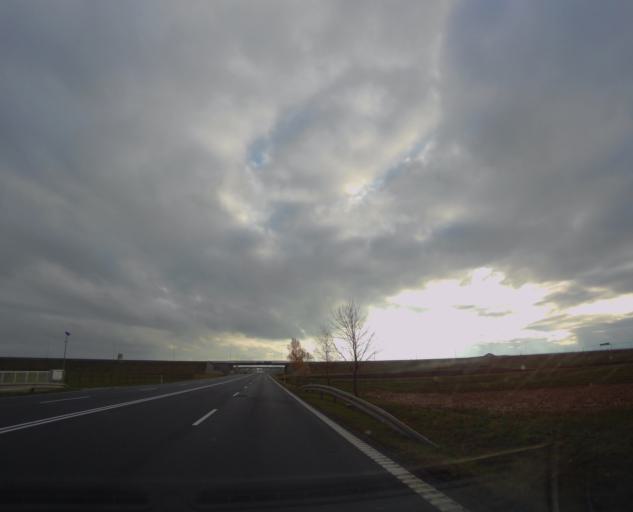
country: PL
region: Subcarpathian Voivodeship
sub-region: Powiat jaroslawski
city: Radymno
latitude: 49.9133
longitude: 22.8191
